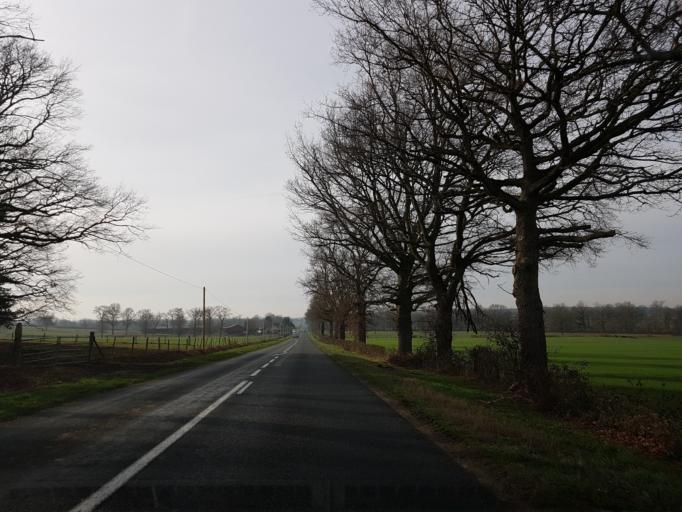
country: FR
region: Auvergne
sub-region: Departement de l'Allier
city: Lusigny
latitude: 46.6026
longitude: 3.5302
